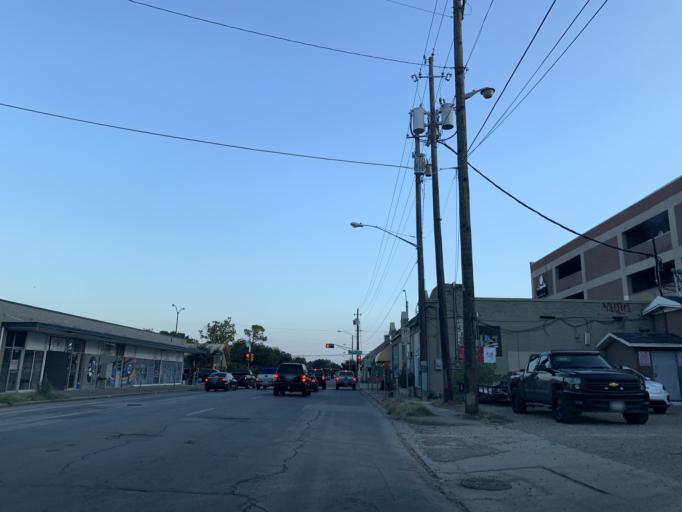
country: US
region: Texas
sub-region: Dallas County
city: Cockrell Hill
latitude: 32.7438
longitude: -96.8395
